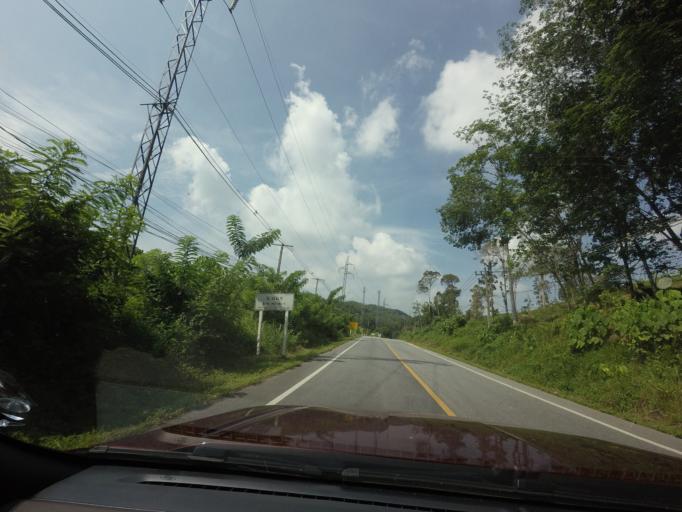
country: TH
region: Yala
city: Betong
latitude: 5.8252
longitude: 101.1121
